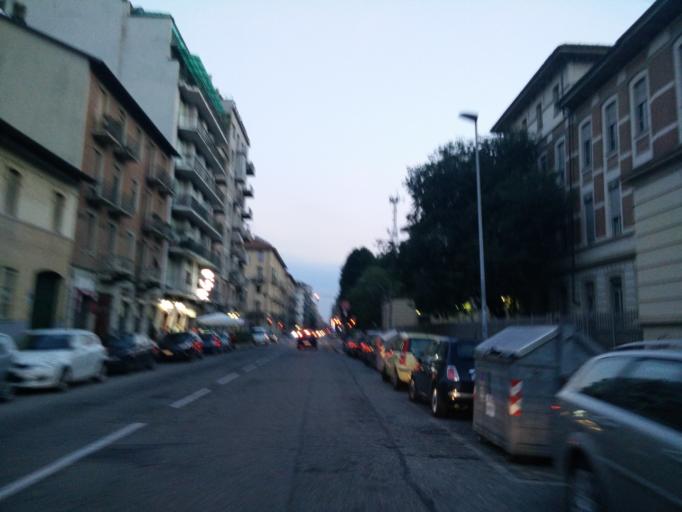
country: IT
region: Piedmont
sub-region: Provincia di Torino
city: Lesna
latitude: 45.0459
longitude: 7.6461
